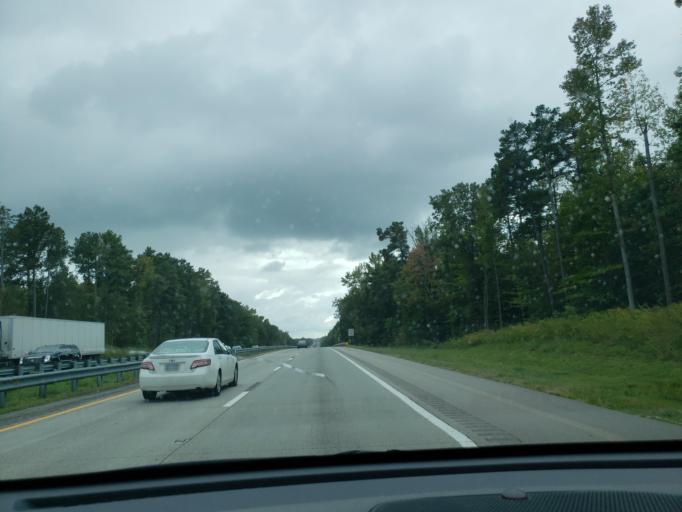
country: US
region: North Carolina
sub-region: Warren County
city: Norlina
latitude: 36.5268
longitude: -78.1971
